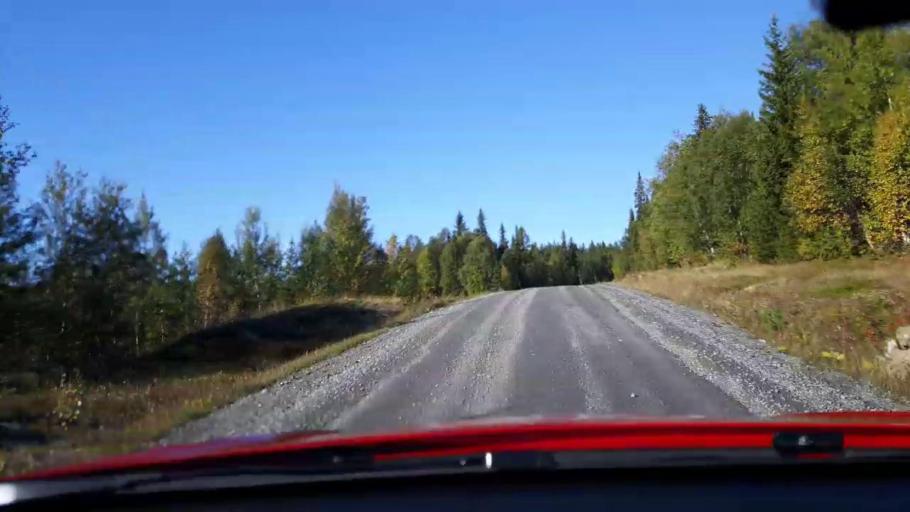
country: NO
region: Nord-Trondelag
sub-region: Lierne
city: Sandvika
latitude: 64.6073
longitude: 13.7146
